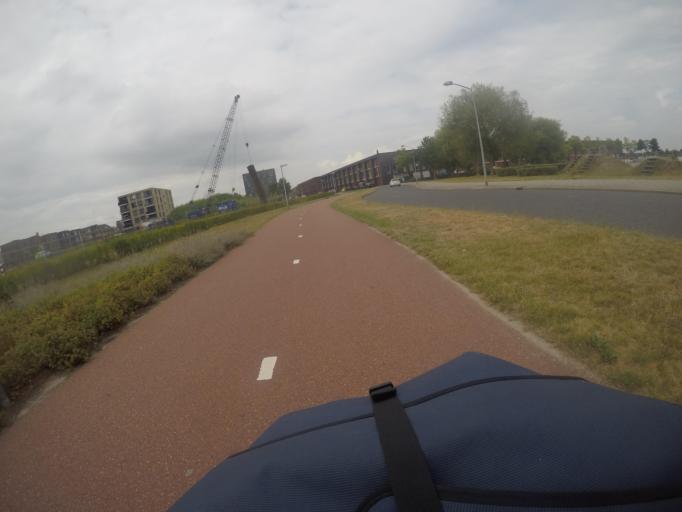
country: NL
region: Flevoland
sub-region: Gemeente Almere
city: Almere Stad
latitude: 52.3911
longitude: 5.1786
